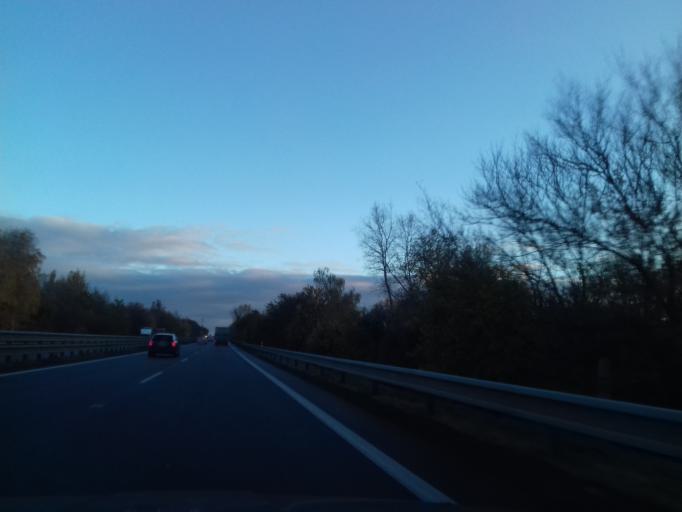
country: CZ
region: South Moravian
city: Pustimer
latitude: 49.3392
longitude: 17.0636
